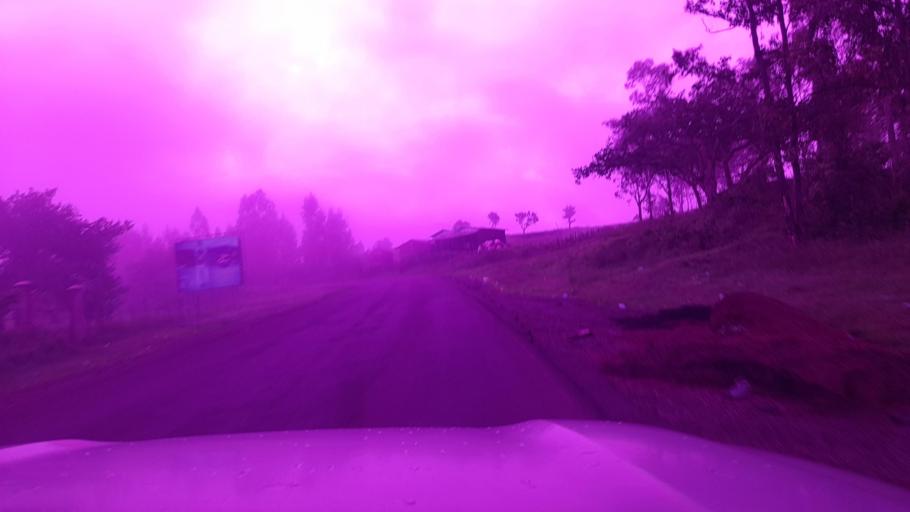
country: ET
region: Oromiya
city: Waliso
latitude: 8.1747
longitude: 37.5595
